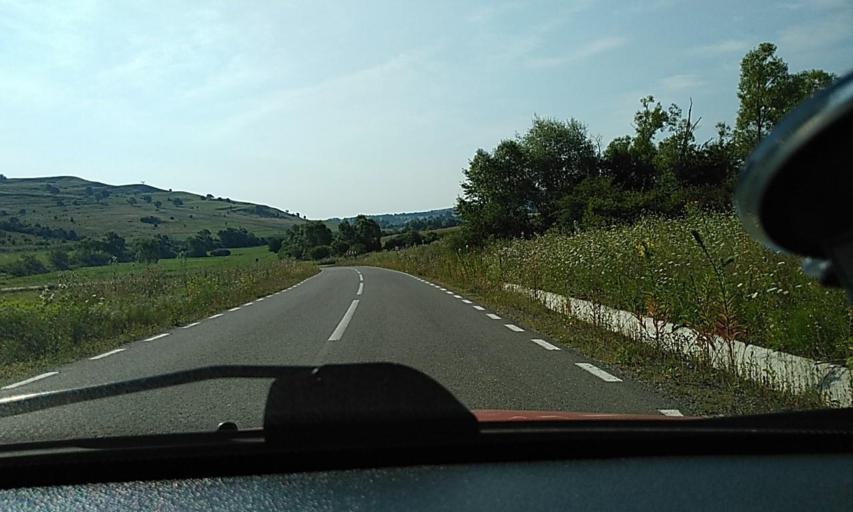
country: RO
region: Brasov
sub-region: Comuna Bunesti
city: Bunesti
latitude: 46.0829
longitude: 25.0607
